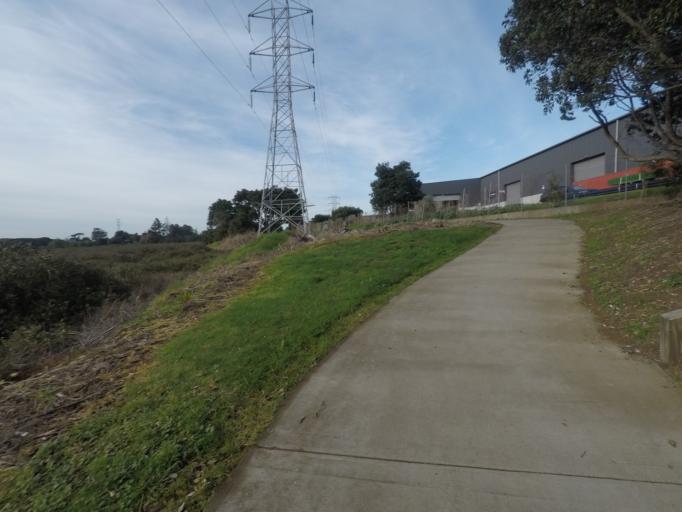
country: NZ
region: Auckland
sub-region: Auckland
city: Mangere
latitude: -36.9454
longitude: 174.7988
